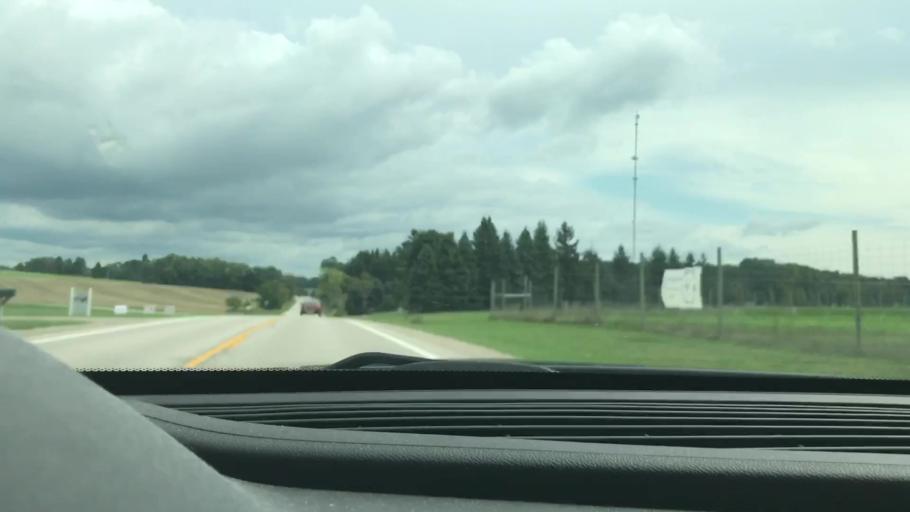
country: US
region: Michigan
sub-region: Antrim County
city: Bellaire
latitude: 45.0969
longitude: -85.2994
